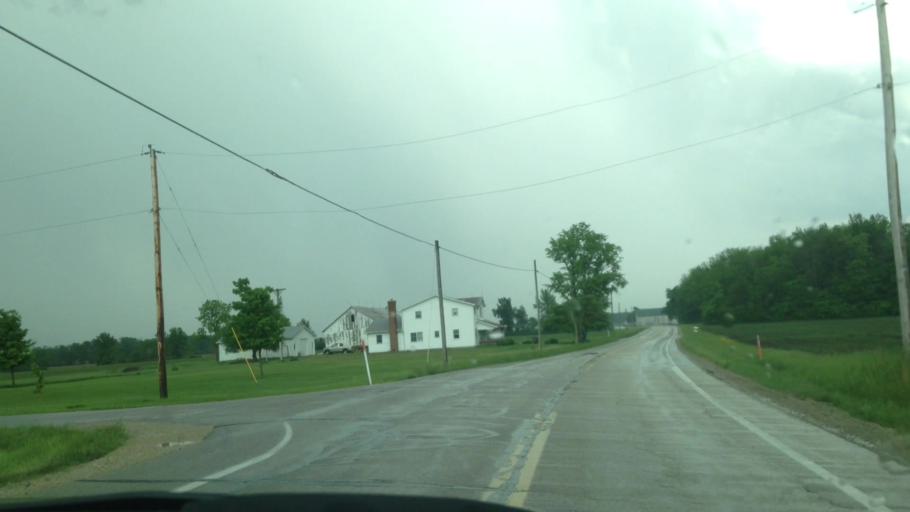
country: US
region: Ohio
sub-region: Darke County
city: Greenville
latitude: 40.1507
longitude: -84.6640
